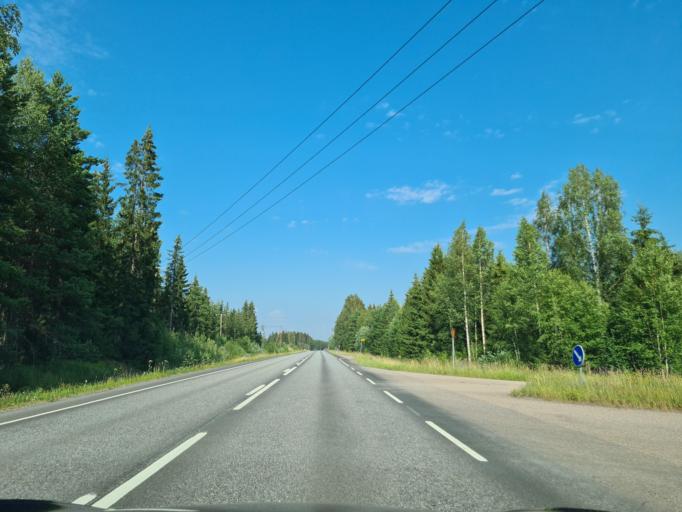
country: FI
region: Satakunta
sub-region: Pori
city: Laengelmaeki
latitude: 61.7786
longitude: 22.1974
